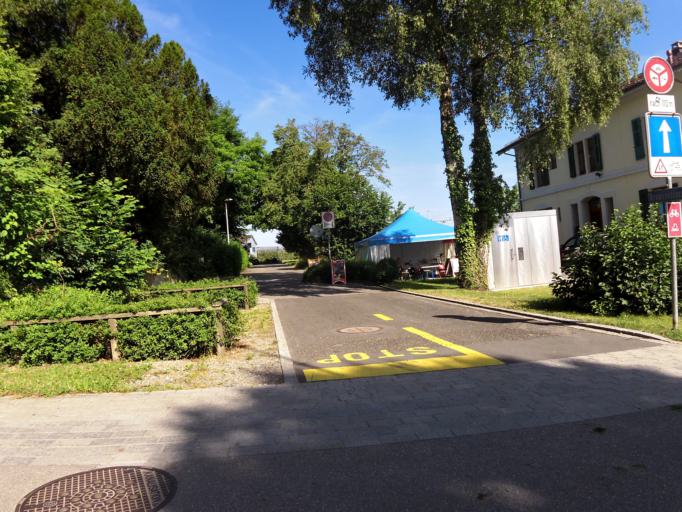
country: CH
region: Thurgau
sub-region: Kreuzlingen District
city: Altnau
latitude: 47.6211
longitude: 9.2660
